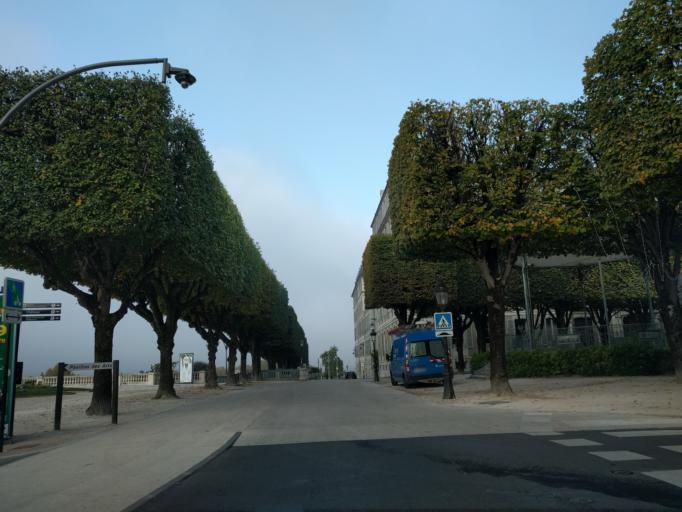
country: FR
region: Aquitaine
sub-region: Departement des Pyrenees-Atlantiques
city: Pau
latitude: 43.2934
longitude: -0.3706
